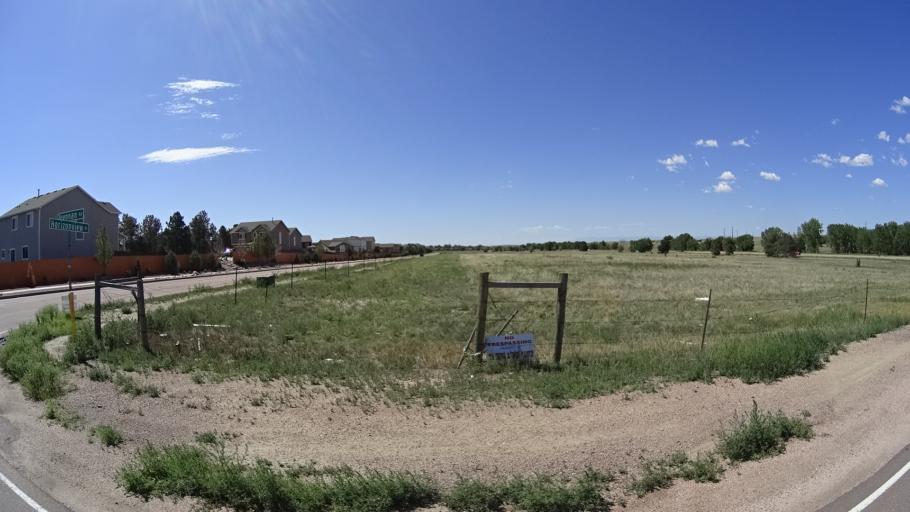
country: US
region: Colorado
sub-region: El Paso County
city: Security-Widefield
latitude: 38.7809
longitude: -104.6579
